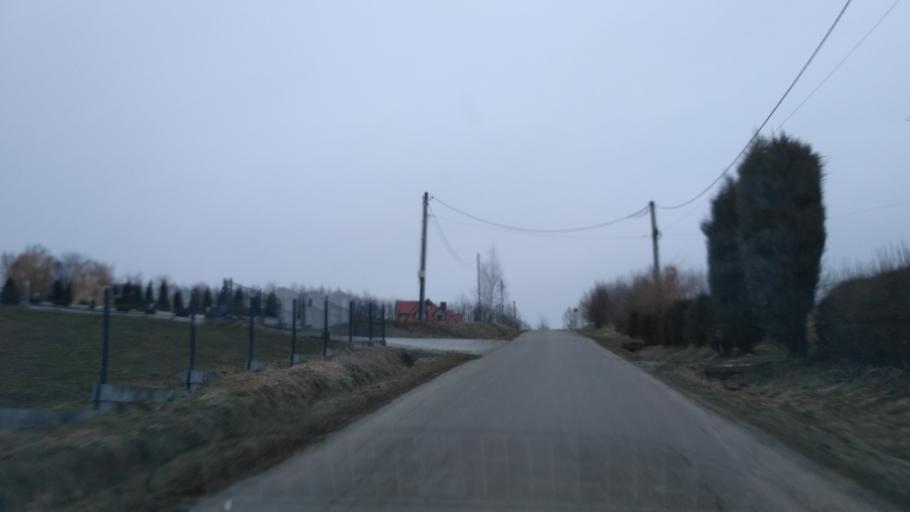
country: PL
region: Subcarpathian Voivodeship
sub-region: Powiat rzeszowski
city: Chmielnik
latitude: 49.9793
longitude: 22.1463
